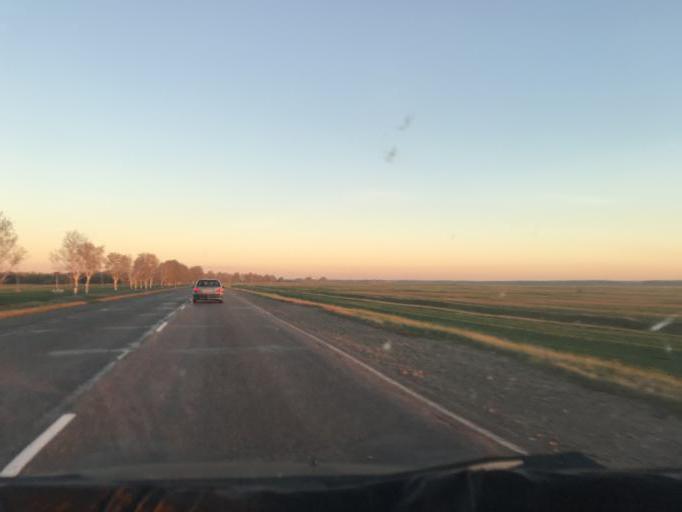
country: BY
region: Gomel
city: Kalinkavichy
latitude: 52.1618
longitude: 29.2297
